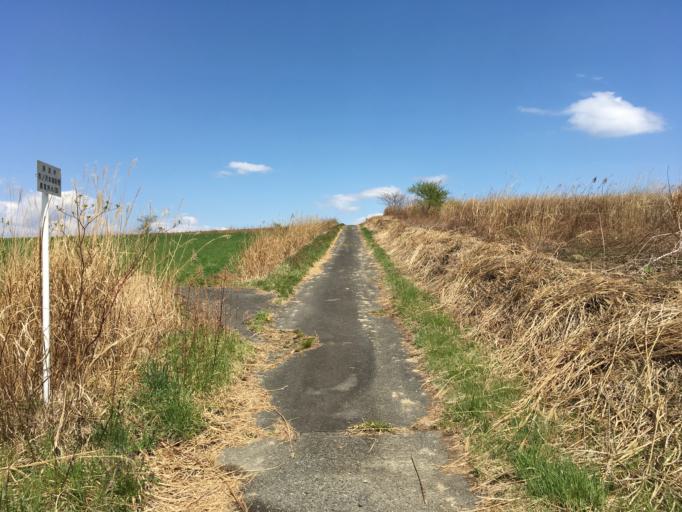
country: JP
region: Iwate
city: Ichinoseki
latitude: 38.8057
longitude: 141.2605
